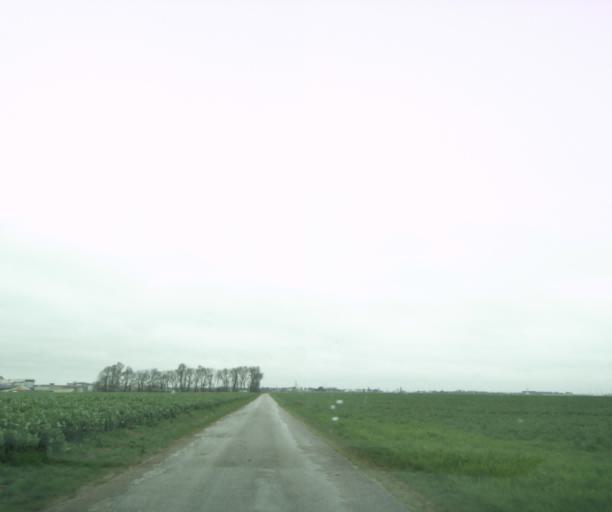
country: FR
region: Centre
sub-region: Departement du Loiret
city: Artenay
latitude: 48.0953
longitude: 1.8773
